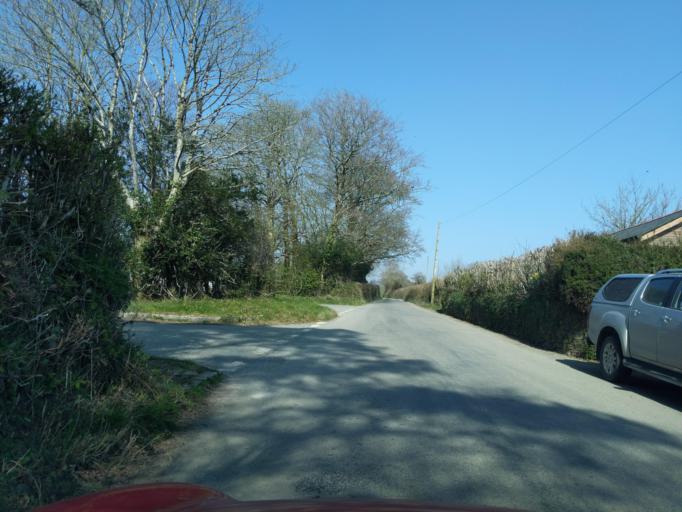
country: GB
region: England
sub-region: Devon
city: Horrabridge
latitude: 50.4775
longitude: -4.1315
